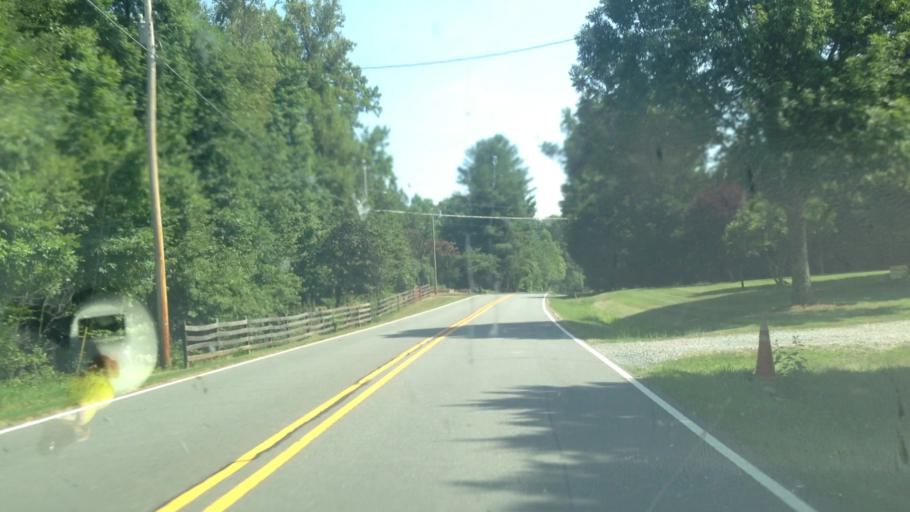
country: US
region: North Carolina
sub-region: Stokes County
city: Danbury
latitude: 36.3970
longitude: -80.0949
